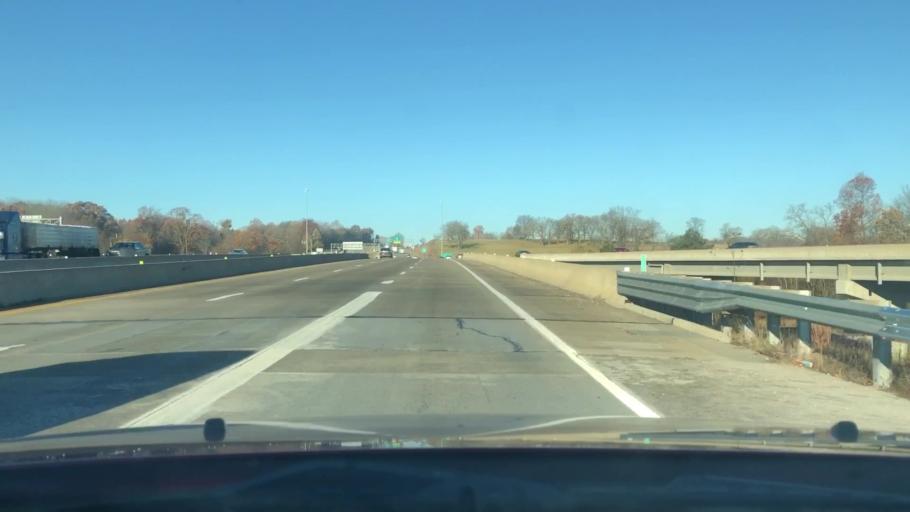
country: US
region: Missouri
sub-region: Christian County
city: Nixa
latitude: 37.1296
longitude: -93.2341
